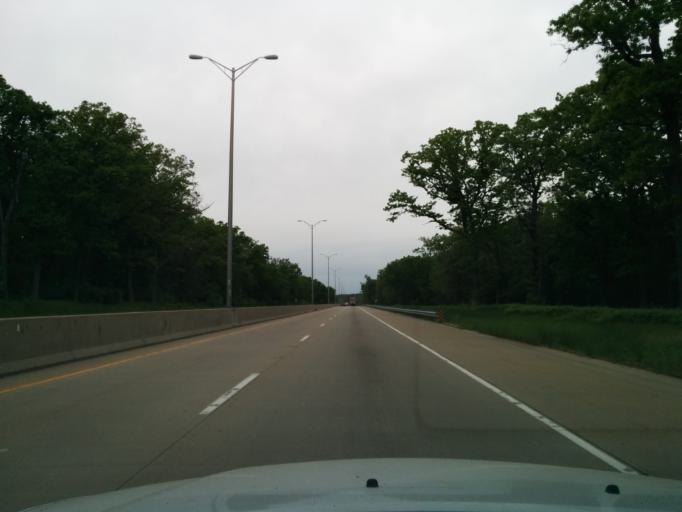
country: US
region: Illinois
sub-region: Cook County
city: Willow Springs
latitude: 41.7244
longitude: -87.8520
